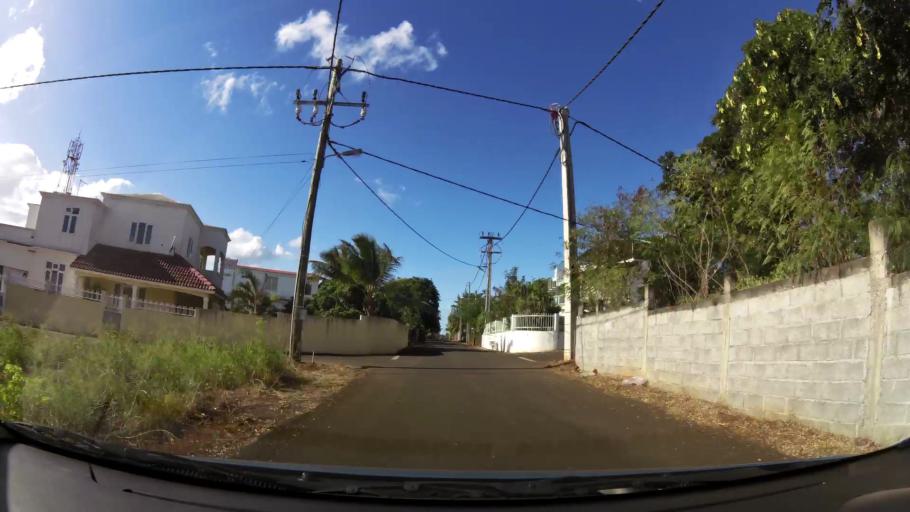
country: MU
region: Black River
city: Albion
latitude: -20.1979
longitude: 57.4083
